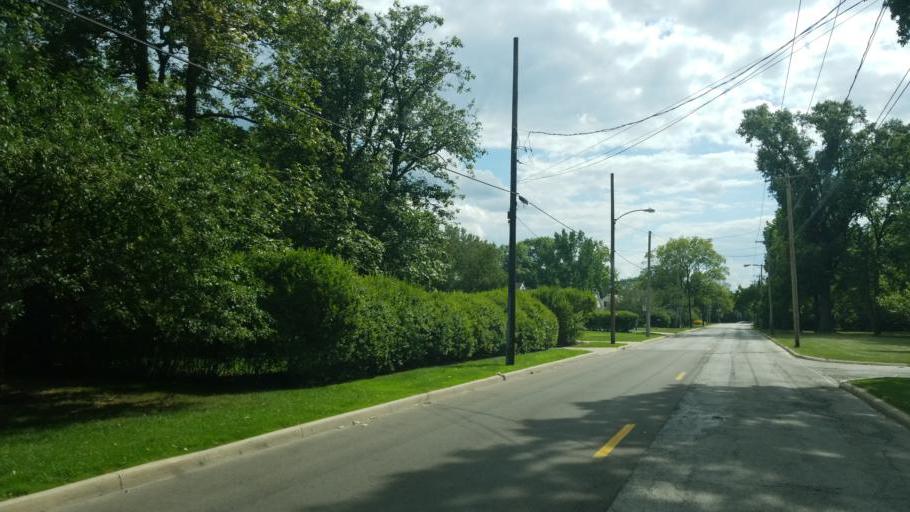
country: US
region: Ohio
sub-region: Wood County
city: Perrysburg
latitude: 41.5844
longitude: -83.6077
